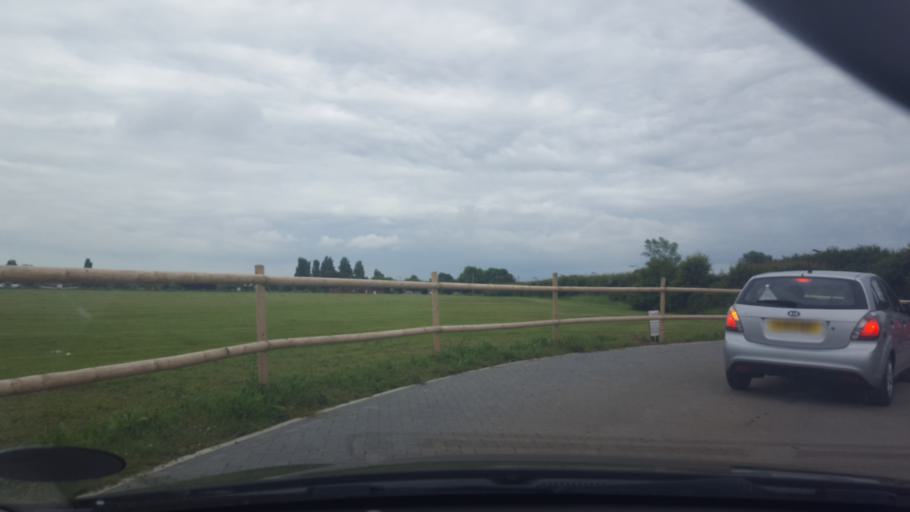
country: GB
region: England
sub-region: Essex
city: Clacton-on-Sea
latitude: 51.7826
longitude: 1.1288
